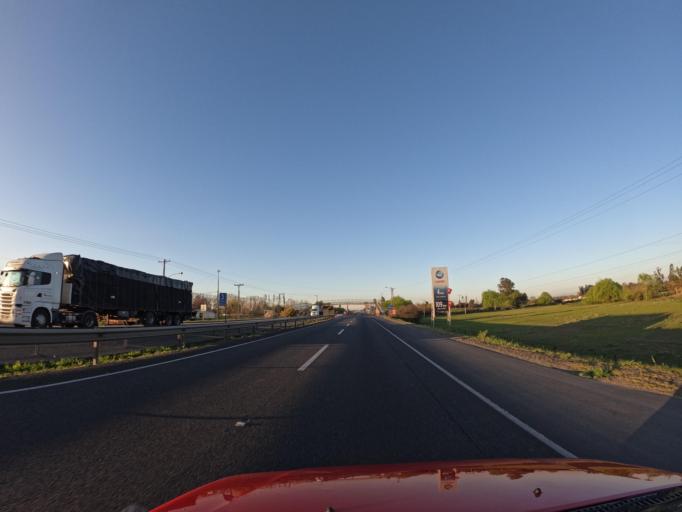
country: CL
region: Biobio
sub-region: Provincia de Nuble
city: San Carlos
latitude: -36.4933
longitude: -72.0280
